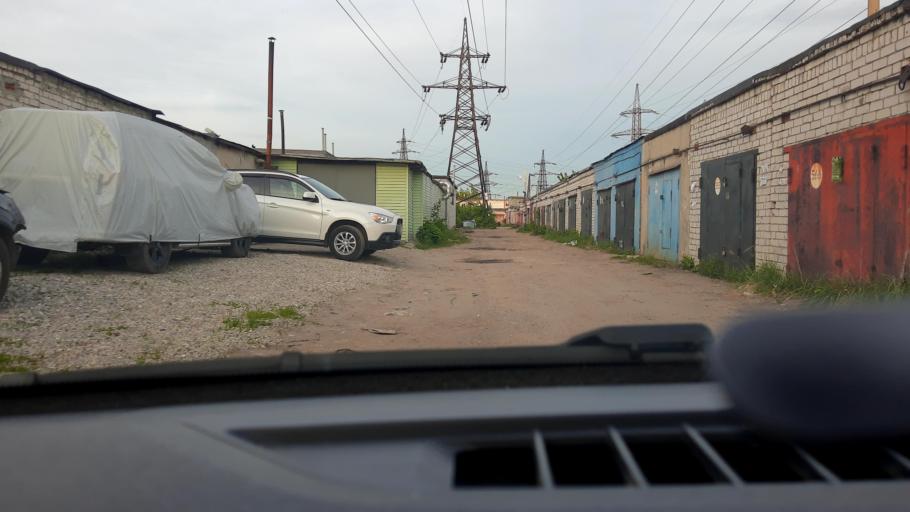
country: RU
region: Nizjnij Novgorod
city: Nizhniy Novgorod
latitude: 56.2823
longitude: 43.8885
